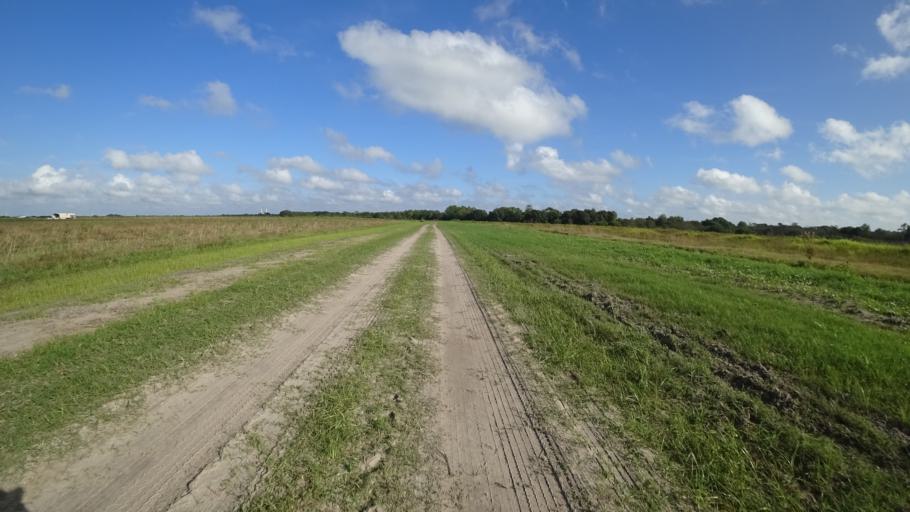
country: US
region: Florida
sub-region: Hillsborough County
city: Wimauma
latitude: 27.5544
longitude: -82.3220
